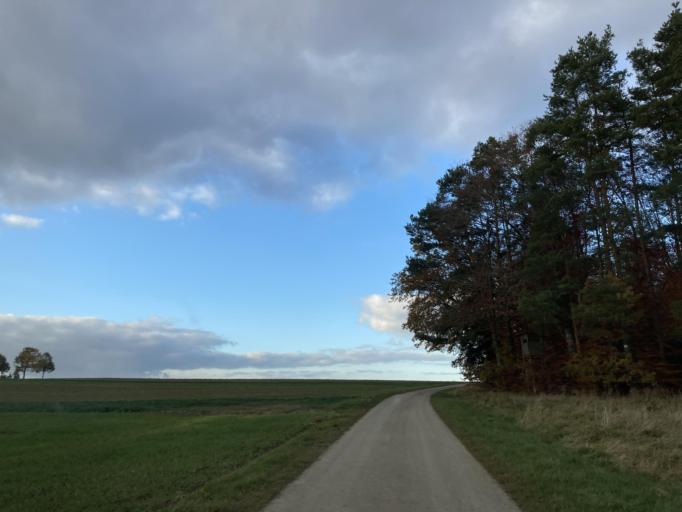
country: DE
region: Baden-Wuerttemberg
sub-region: Tuebingen Region
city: Haigerloch
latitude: 48.4185
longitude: 8.7860
